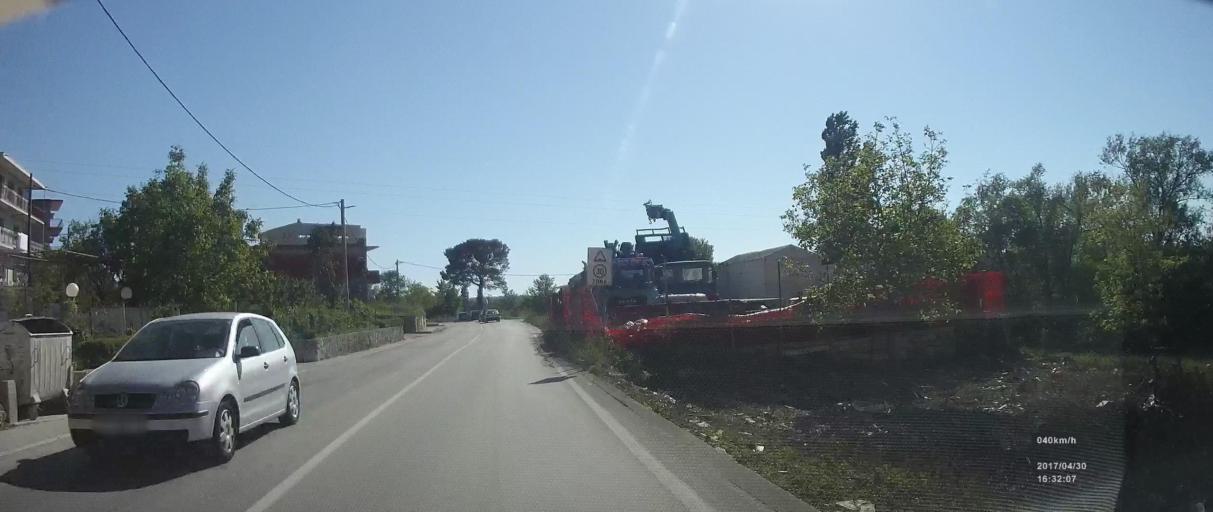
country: HR
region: Splitsko-Dalmatinska
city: Zrnovnica
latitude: 43.5138
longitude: 16.5406
